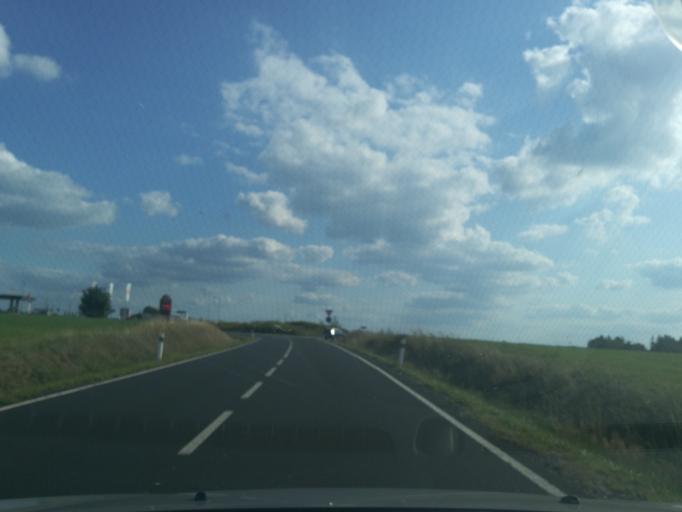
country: CZ
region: Karlovarsky
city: Hranice
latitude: 50.3187
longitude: 12.1664
